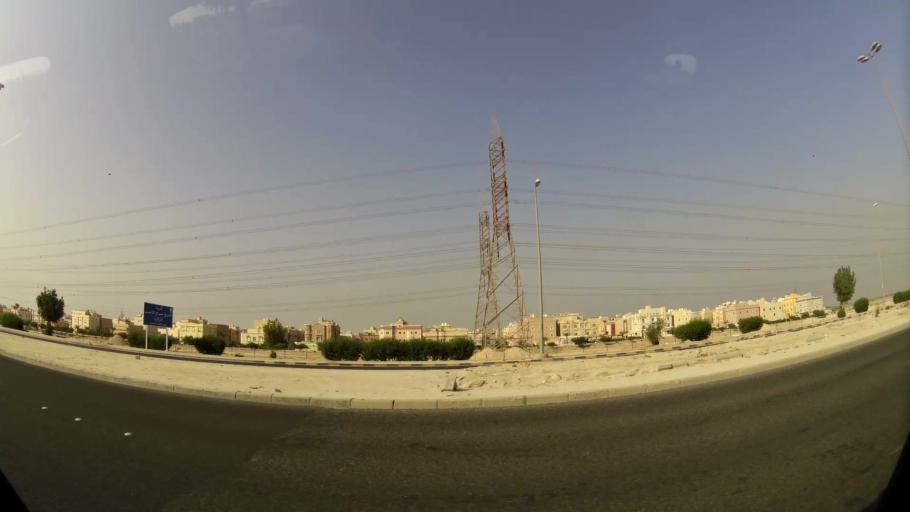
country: KW
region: Al Asimah
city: Ar Rabiyah
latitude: 29.2954
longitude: 47.8139
